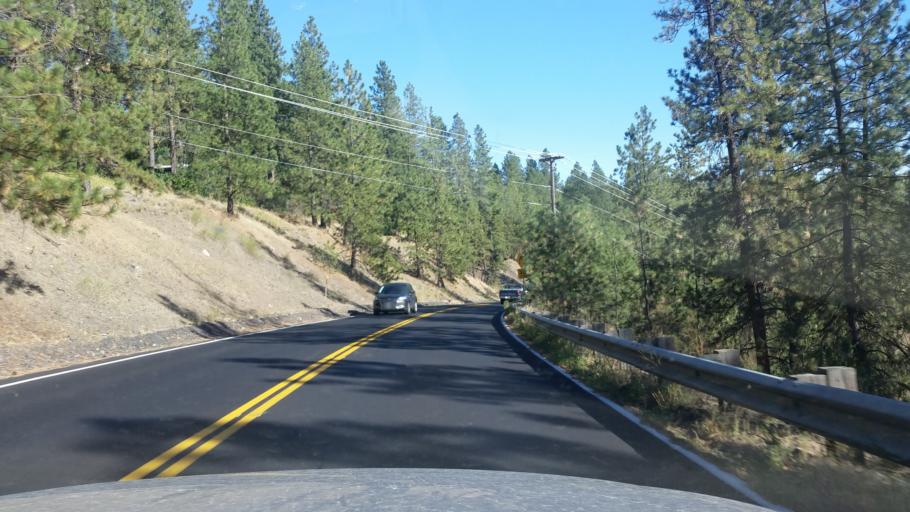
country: US
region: Washington
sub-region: Spokane County
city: Spokane
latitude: 47.6012
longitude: -117.3908
